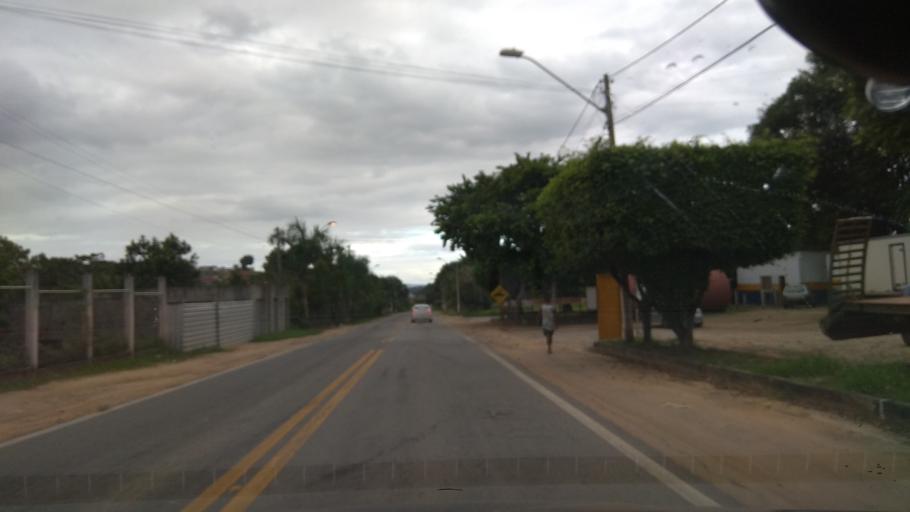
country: BR
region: Bahia
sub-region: Ubata
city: Ubata
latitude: -14.2035
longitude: -39.5317
